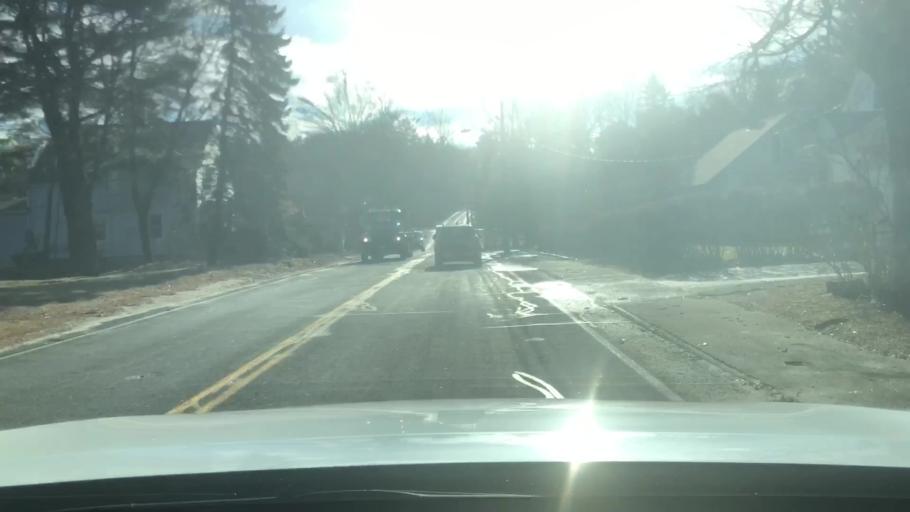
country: US
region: Rhode Island
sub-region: Providence County
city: Woonsocket
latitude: 42.0237
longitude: -71.4872
